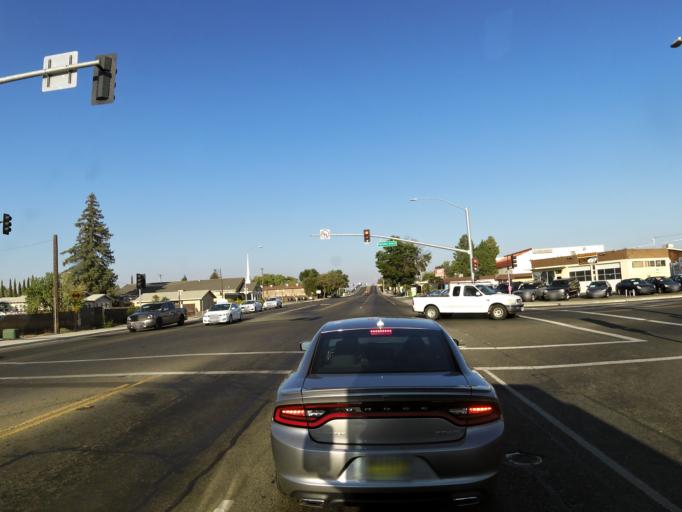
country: US
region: California
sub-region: Merced County
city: Merced
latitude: 37.2951
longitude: -120.4519
